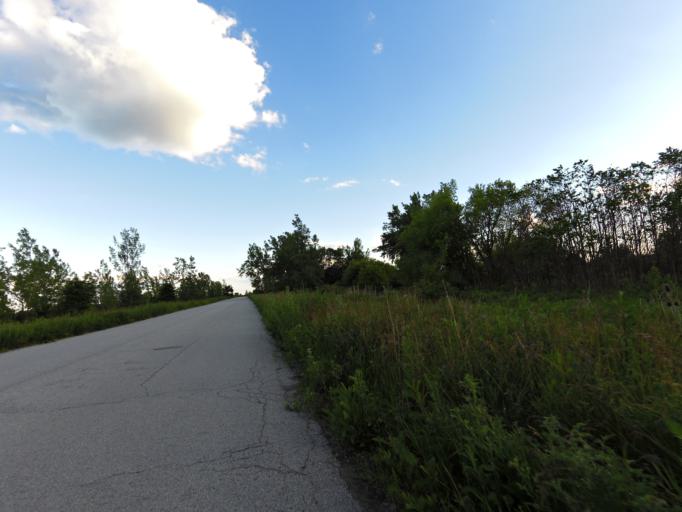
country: CA
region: Ontario
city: Toronto
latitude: 43.6366
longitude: -79.3232
